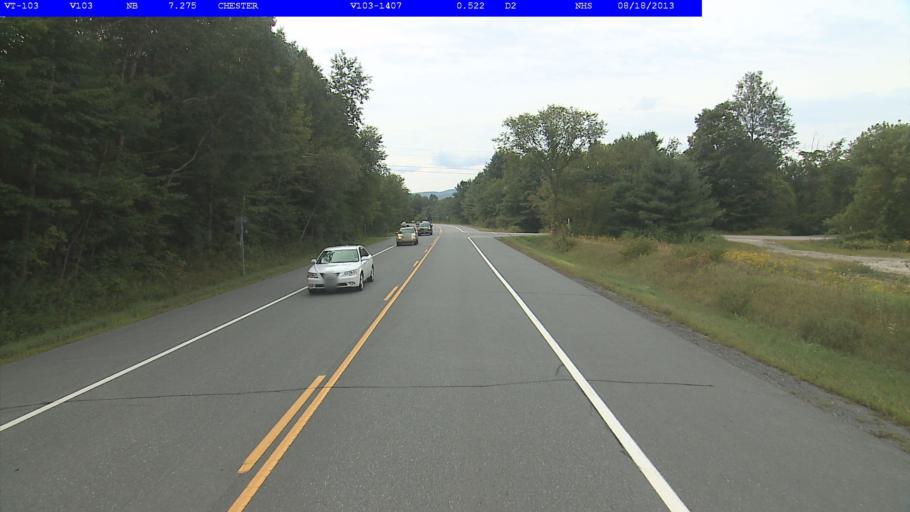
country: US
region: Vermont
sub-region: Windsor County
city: Chester
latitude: 43.2400
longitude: -72.5610
